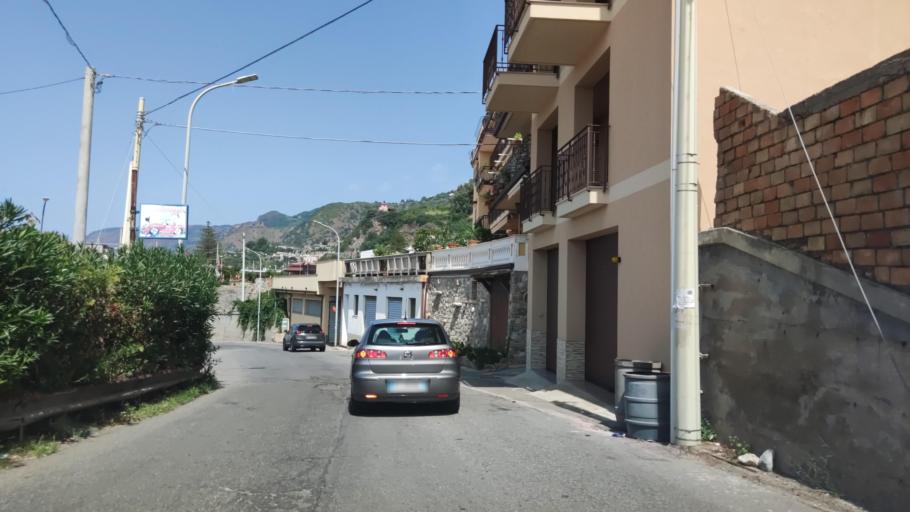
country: IT
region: Calabria
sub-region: Provincia di Reggio Calabria
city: Bagnara Calabra
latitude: 38.2813
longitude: 15.7991
